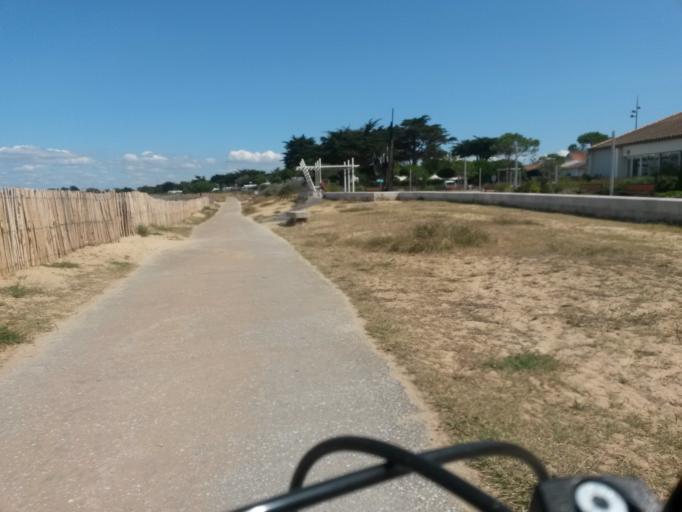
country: FR
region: Poitou-Charentes
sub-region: Departement de la Charente-Maritime
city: Rivedoux-Plage
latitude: 46.1596
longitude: -1.2726
